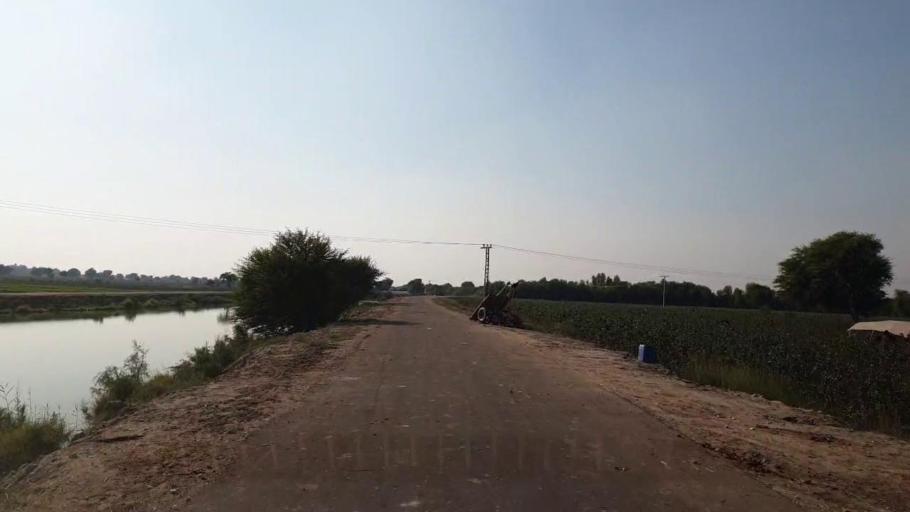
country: PK
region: Sindh
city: Sehwan
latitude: 26.4373
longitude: 67.7933
